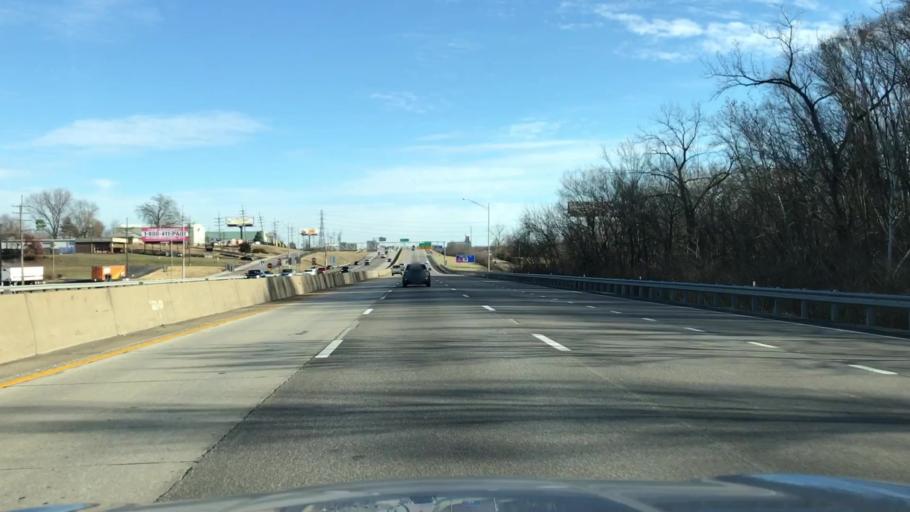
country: US
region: Missouri
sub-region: Saint Louis County
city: Spanish Lake
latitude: 38.7693
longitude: -90.2175
